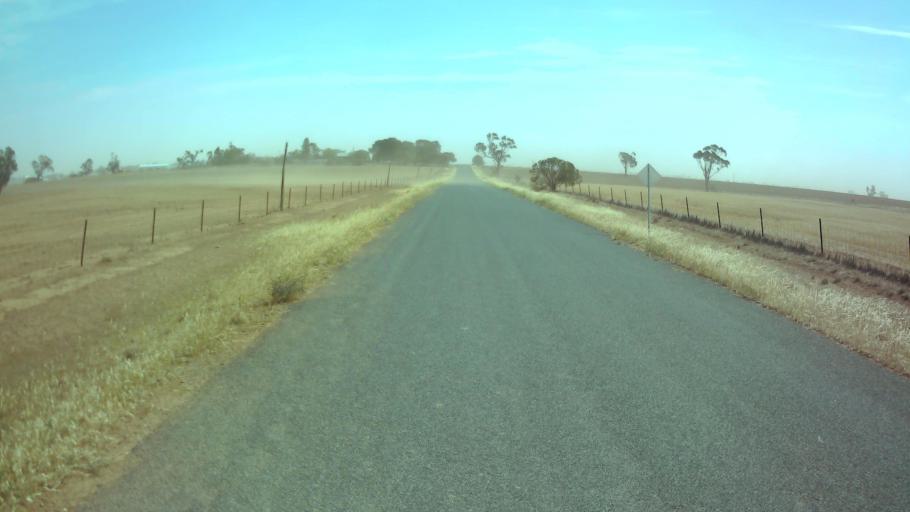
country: AU
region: New South Wales
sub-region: Weddin
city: Grenfell
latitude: -33.7345
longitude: 147.9974
